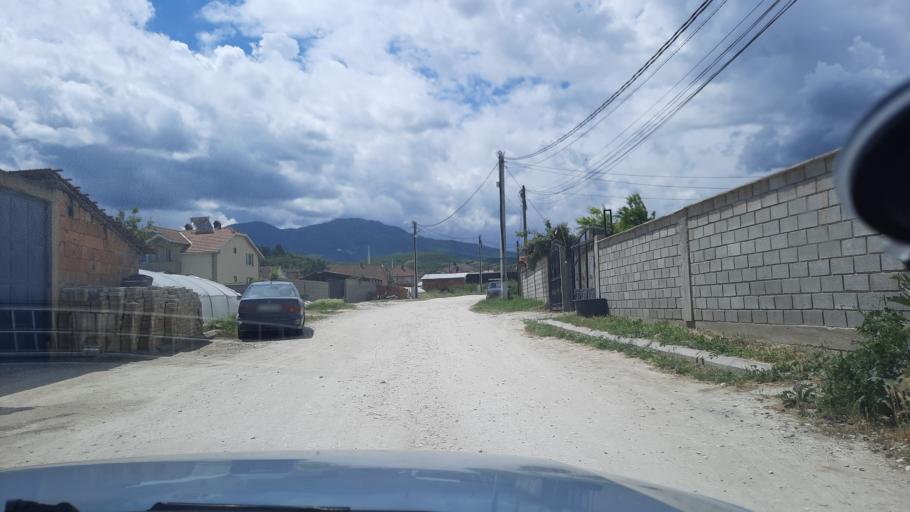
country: MK
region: Studenicani
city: Studenichani
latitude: 41.9250
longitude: 21.5389
